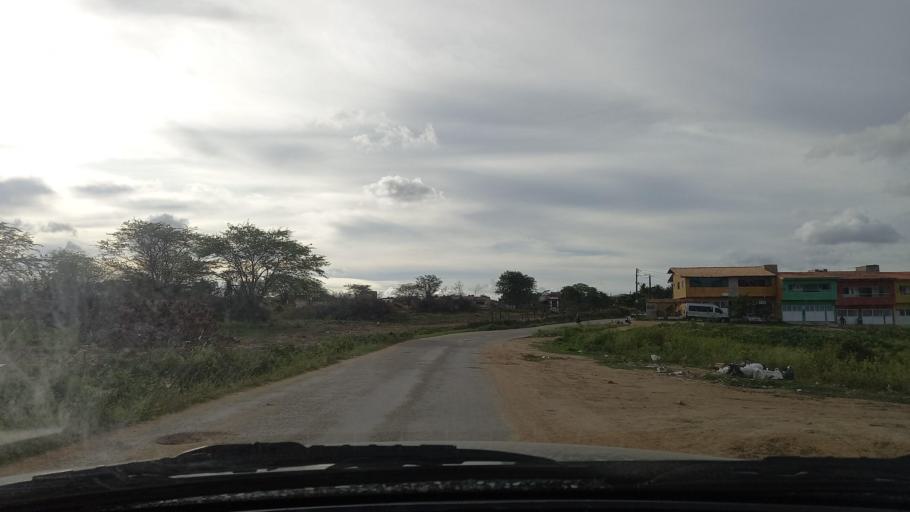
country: BR
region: Pernambuco
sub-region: Gravata
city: Gravata
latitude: -8.2042
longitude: -35.5598
